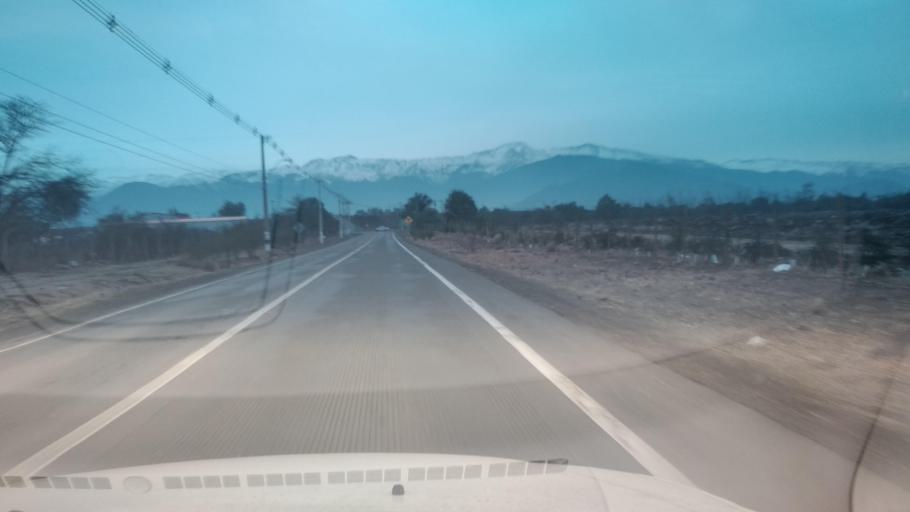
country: CL
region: Santiago Metropolitan
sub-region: Provincia de Chacabuco
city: Chicureo Abajo
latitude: -33.0949
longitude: -70.6963
